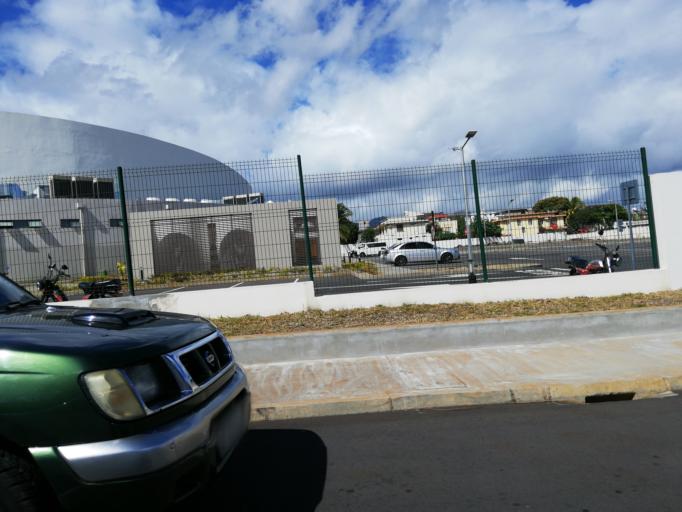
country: MU
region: Moka
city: Pailles
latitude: -20.1906
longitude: 57.4685
